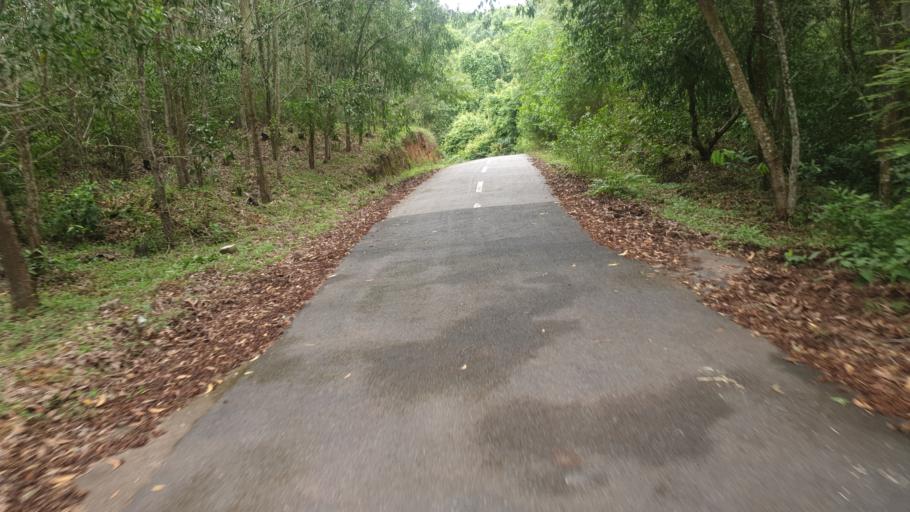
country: IN
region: Kerala
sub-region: Thiruvananthapuram
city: Nedumangad
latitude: 8.6299
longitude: 77.1254
